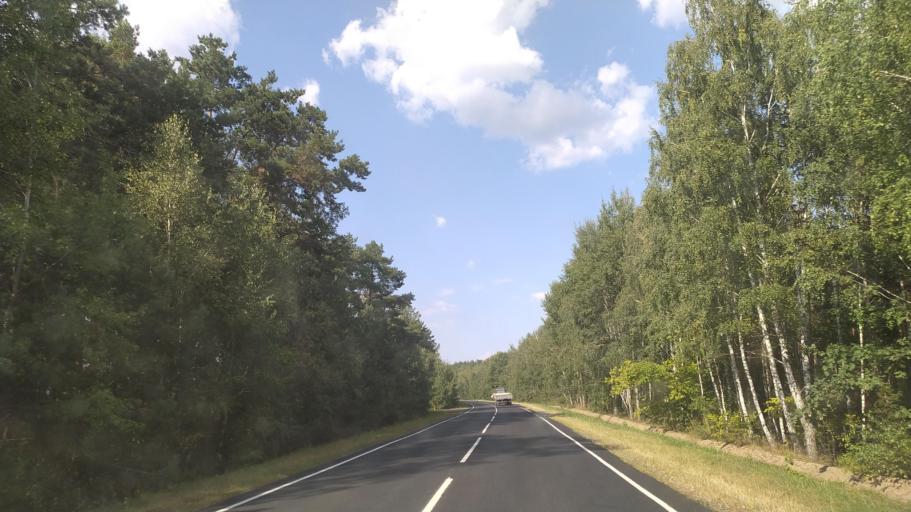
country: BY
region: Brest
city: Drahichyn
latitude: 52.2733
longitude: 25.0714
